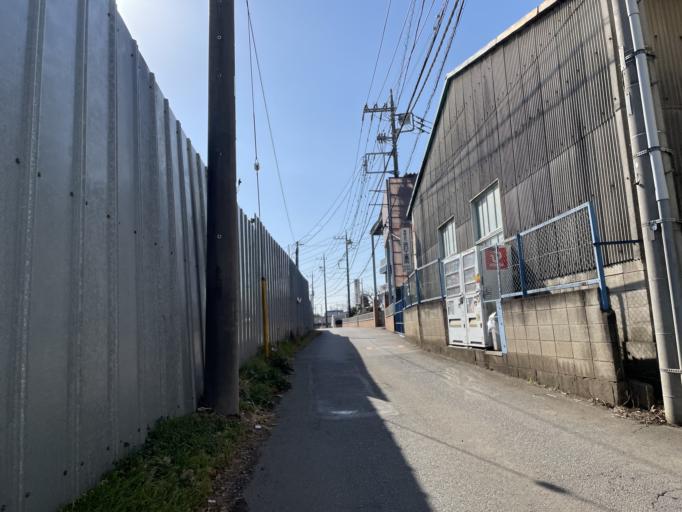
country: JP
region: Saitama
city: Oi
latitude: 35.8212
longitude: 139.5333
